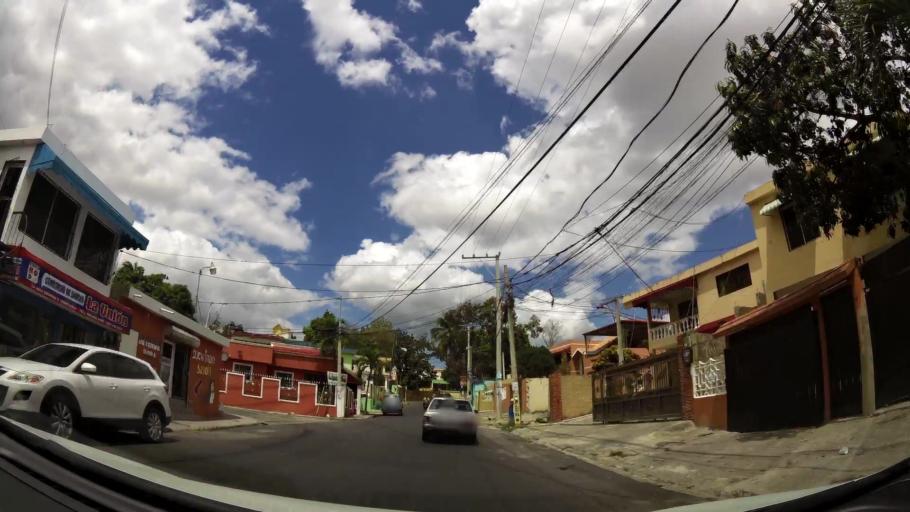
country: DO
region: Nacional
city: Ensanche Luperon
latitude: 18.5237
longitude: -69.9098
